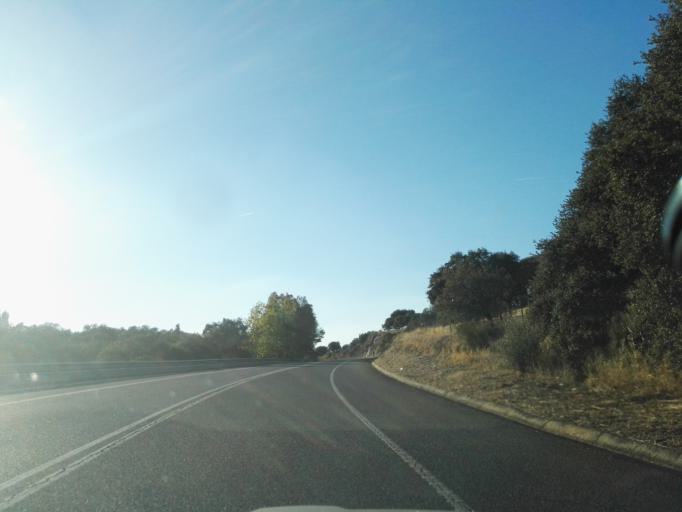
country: PT
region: Evora
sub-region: Vila Vicosa
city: Vila Vicosa
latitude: 38.8454
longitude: -7.3772
